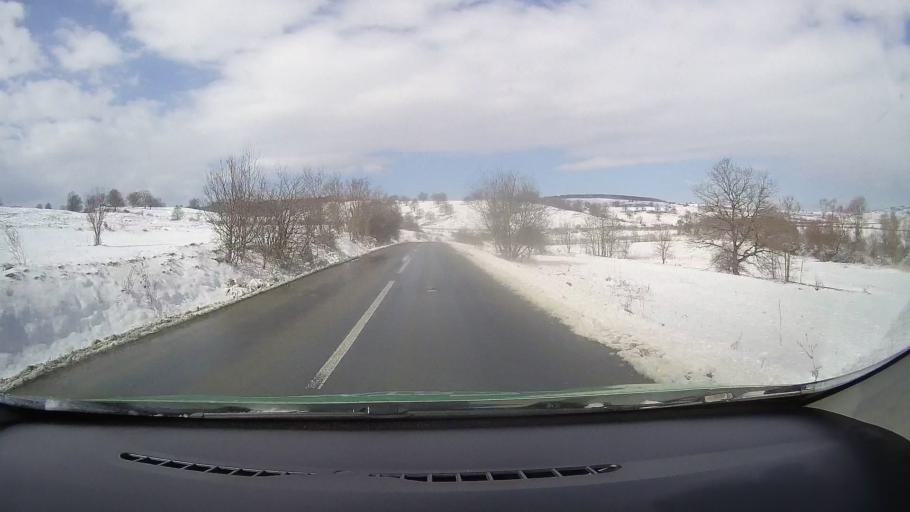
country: RO
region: Sibiu
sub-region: Comuna Altina
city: Altina
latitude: 45.9432
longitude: 24.4530
